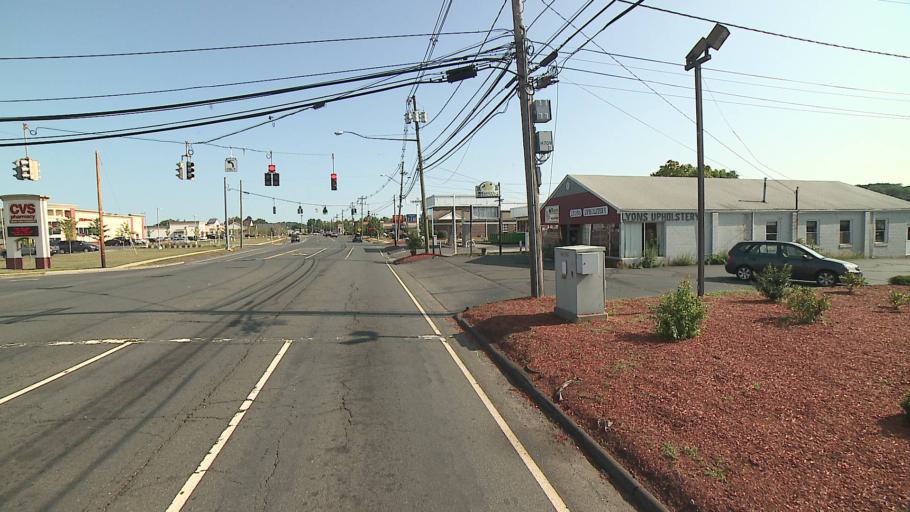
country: US
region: Connecticut
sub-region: New Haven County
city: Wallingford
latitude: 41.4800
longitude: -72.8108
